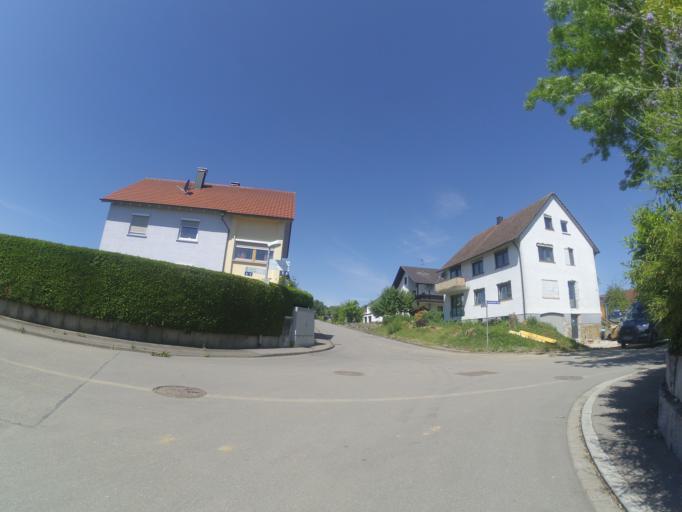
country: DE
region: Baden-Wuerttemberg
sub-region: Tuebingen Region
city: Dornstadt
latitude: 48.4806
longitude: 9.9144
